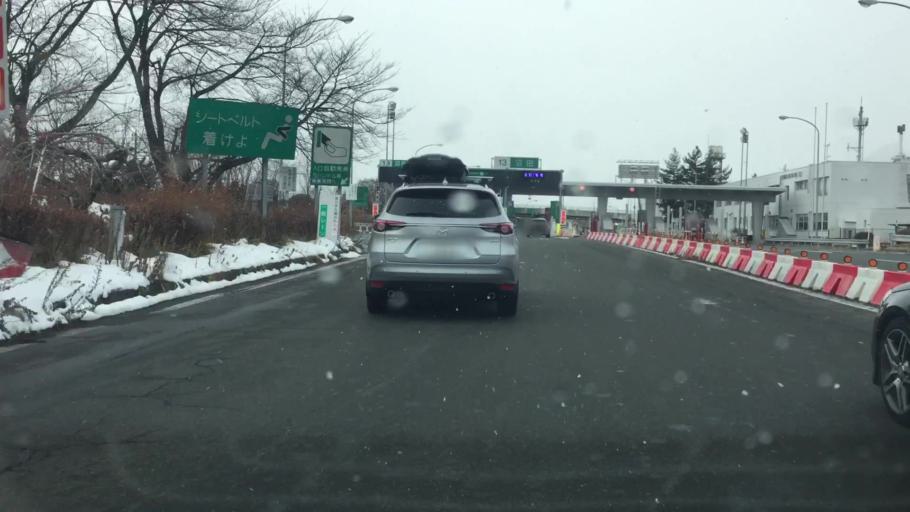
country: JP
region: Gunma
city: Numata
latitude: 36.6542
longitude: 139.0707
